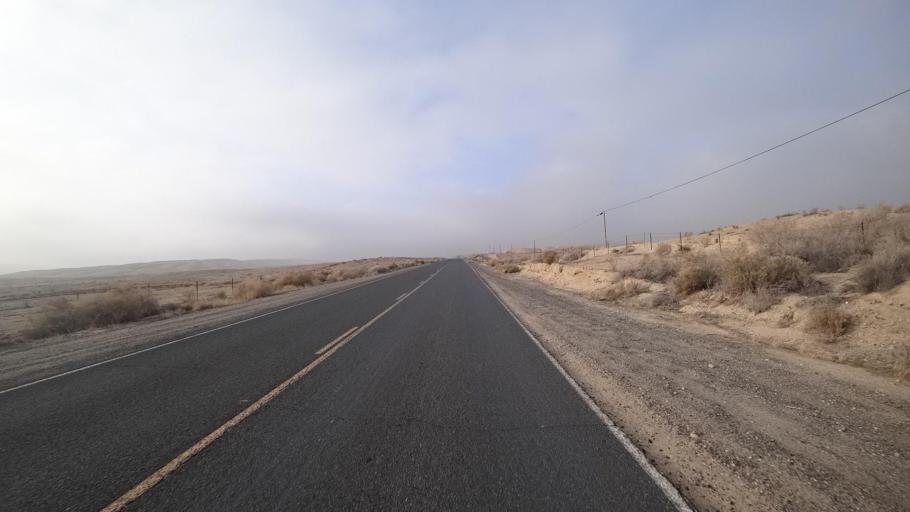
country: US
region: California
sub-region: Kern County
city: Ford City
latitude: 35.2401
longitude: -119.4511
